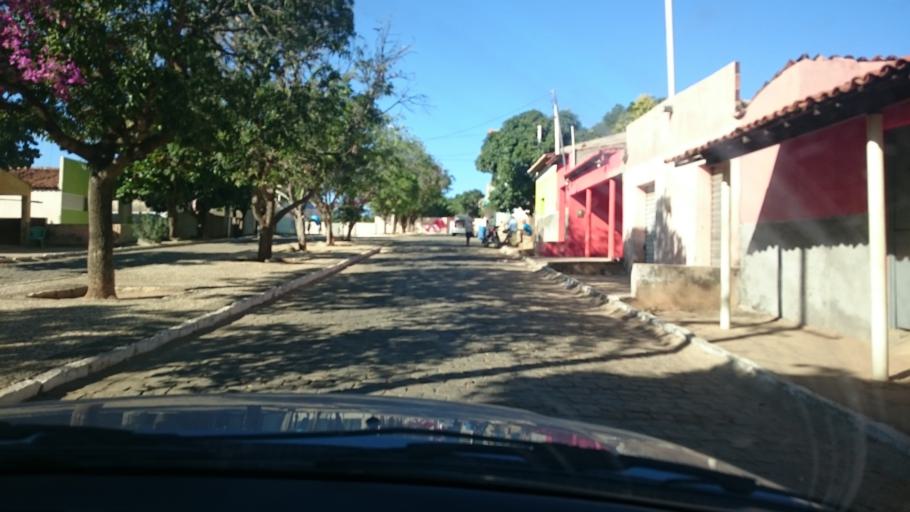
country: BR
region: Paraiba
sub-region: Catole Do Rocha
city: Sao Bento
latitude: -6.1630
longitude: -37.7624
